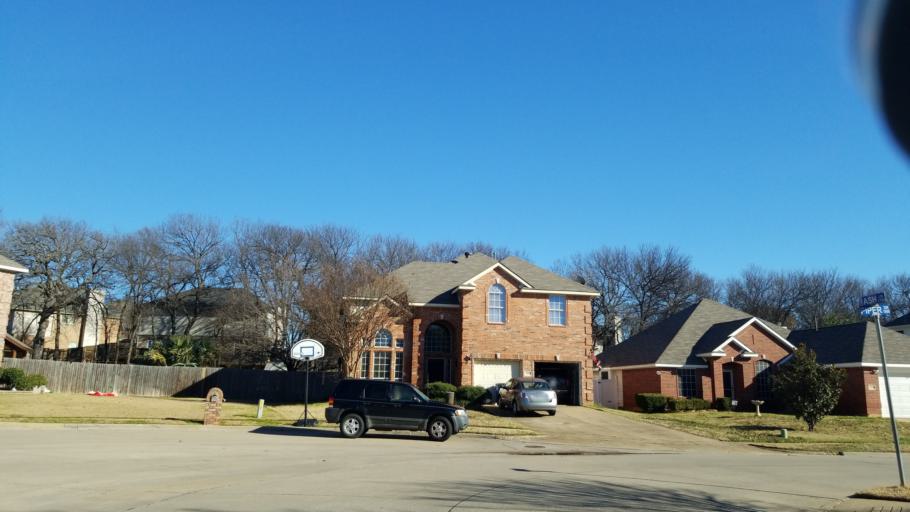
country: US
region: Texas
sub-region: Denton County
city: Corinth
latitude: 33.1417
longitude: -97.0816
